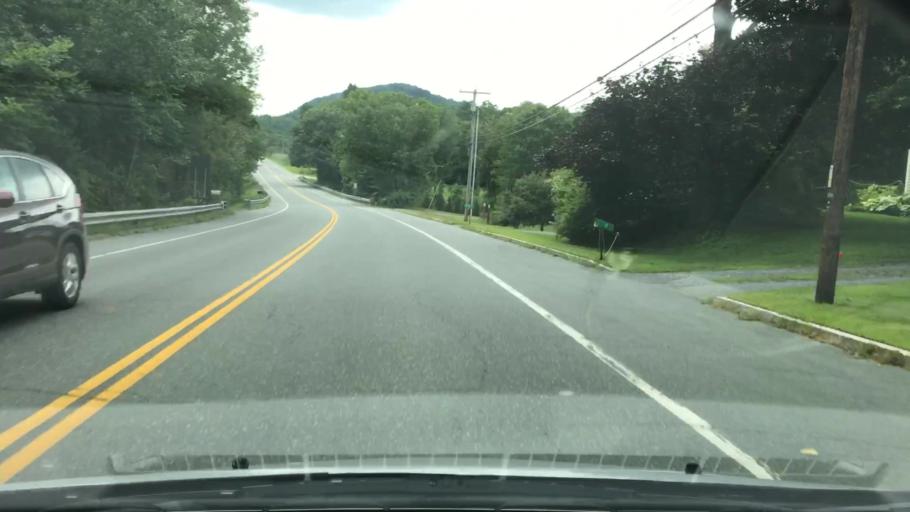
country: US
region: New Hampshire
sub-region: Grafton County
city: Lyme
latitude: 43.8084
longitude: -72.1621
